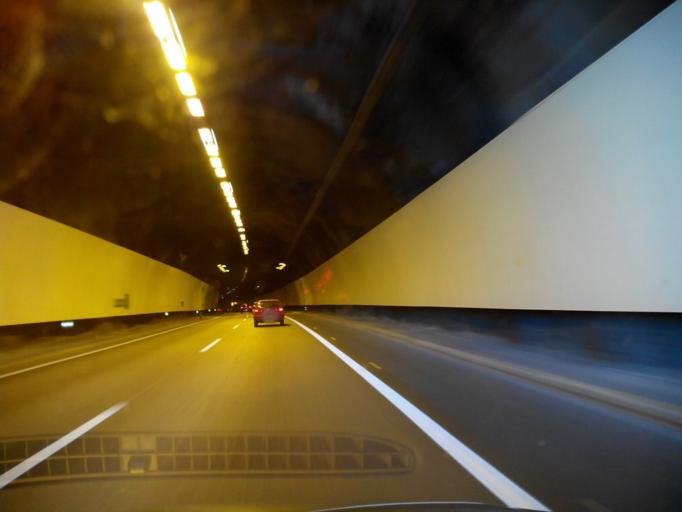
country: ES
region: Catalonia
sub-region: Provincia de Barcelona
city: La Roca del Valles
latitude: 41.5863
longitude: 2.3527
